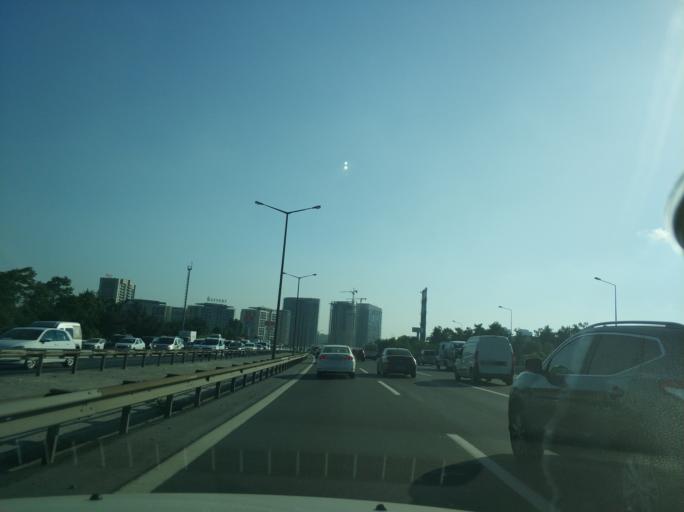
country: TR
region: Istanbul
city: Sisli
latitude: 41.0966
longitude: 28.9525
